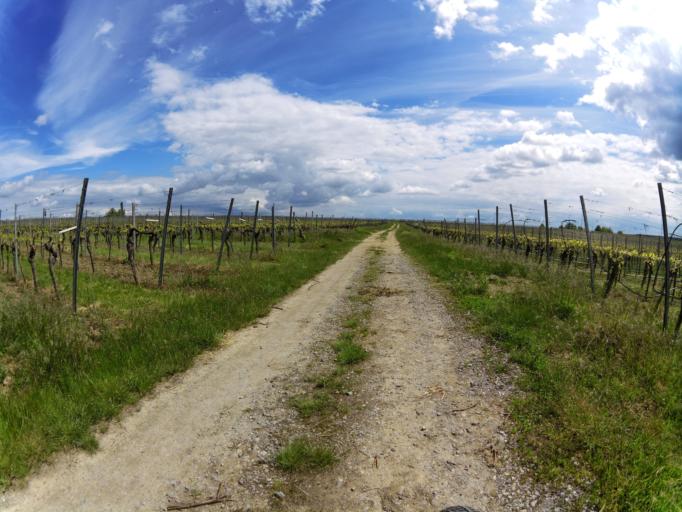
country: DE
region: Bavaria
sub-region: Regierungsbezirk Unterfranken
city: Sommerach
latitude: 49.8444
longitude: 10.1913
